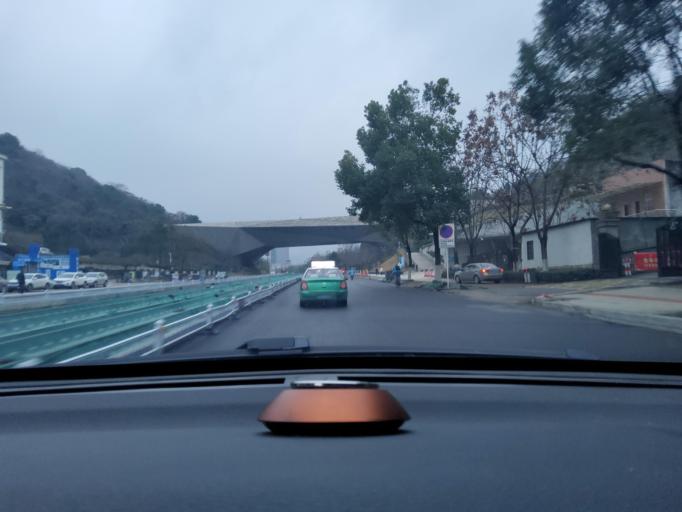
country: CN
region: Hubei
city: Tuanchengshan
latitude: 30.1946
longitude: 115.0214
